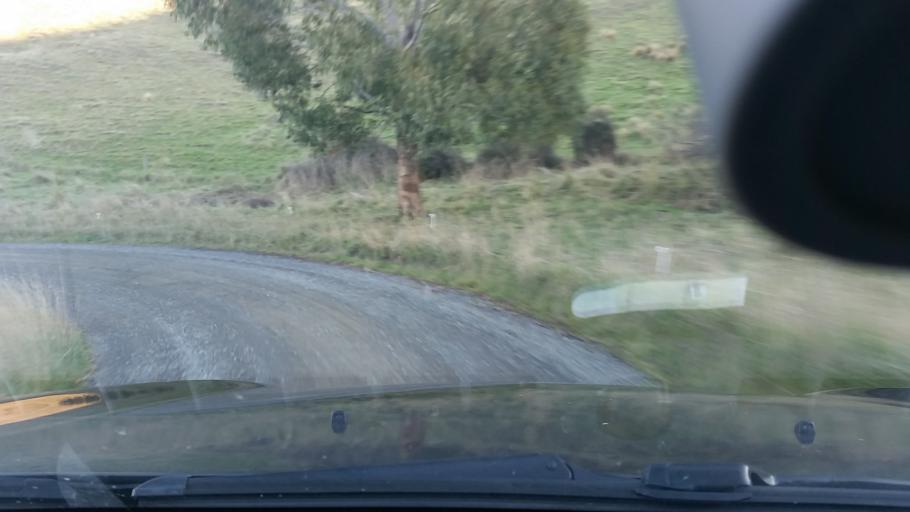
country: NZ
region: Marlborough
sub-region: Marlborough District
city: Blenheim
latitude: -41.7416
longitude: 174.0491
